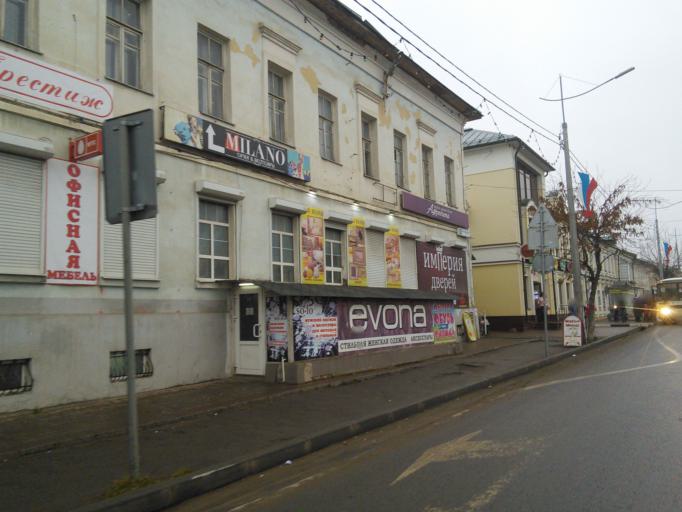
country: RU
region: Jaroslavl
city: Pereslavl'-Zalesskiy
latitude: 56.7396
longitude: 38.8558
